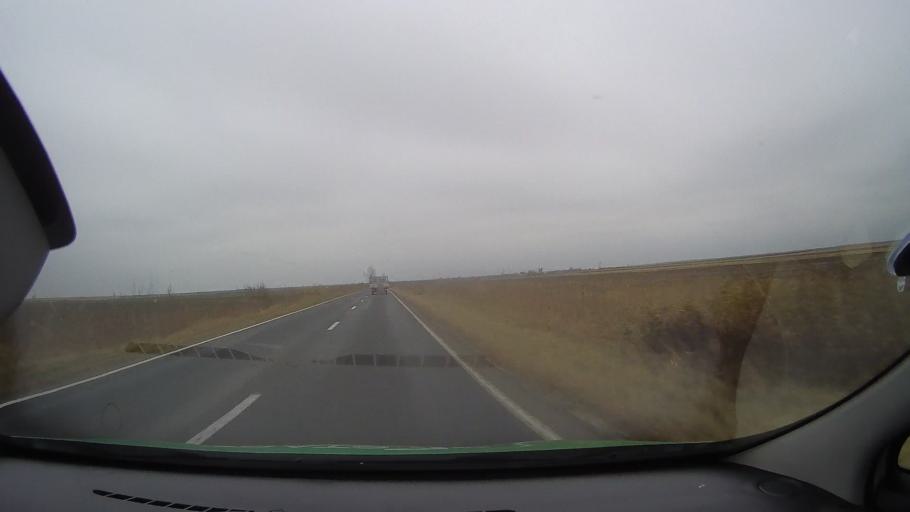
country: RO
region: Ialomita
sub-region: Comuna Scanteia
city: Scanteia
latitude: 44.7444
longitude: 27.4433
